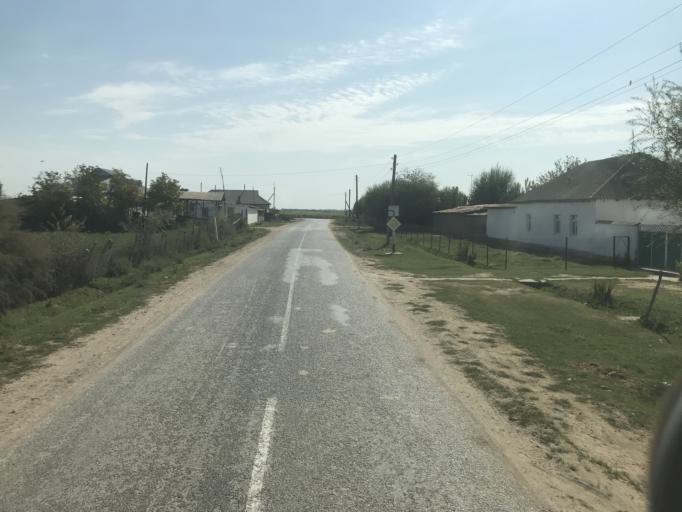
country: KZ
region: Ongtustik Qazaqstan
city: Myrzakent
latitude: 40.6641
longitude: 68.6310
